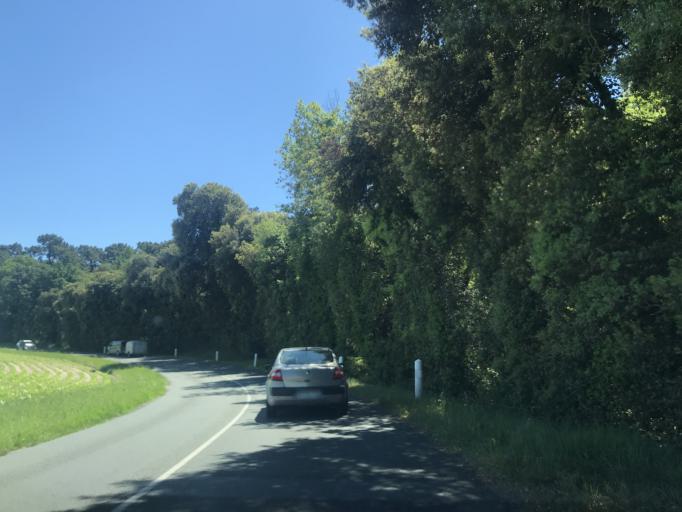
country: FR
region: Poitou-Charentes
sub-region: Departement de la Charente-Maritime
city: Meschers-sur-Gironde
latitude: 45.5914
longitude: -0.9651
